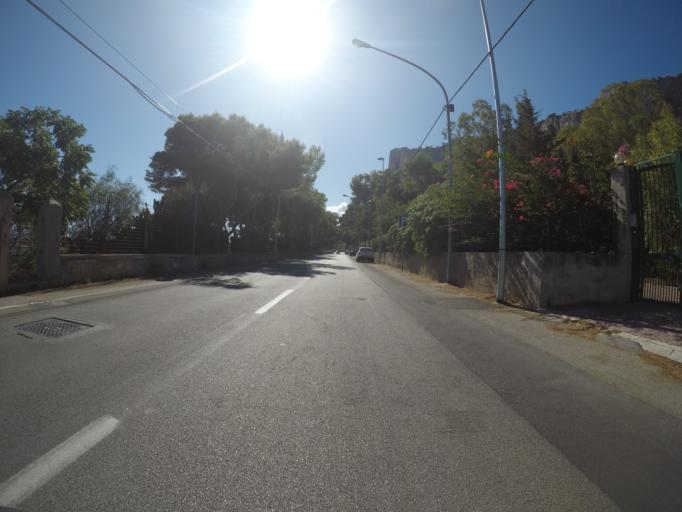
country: IT
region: Sicily
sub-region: Palermo
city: Palermo
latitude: 38.1891
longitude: 13.3593
